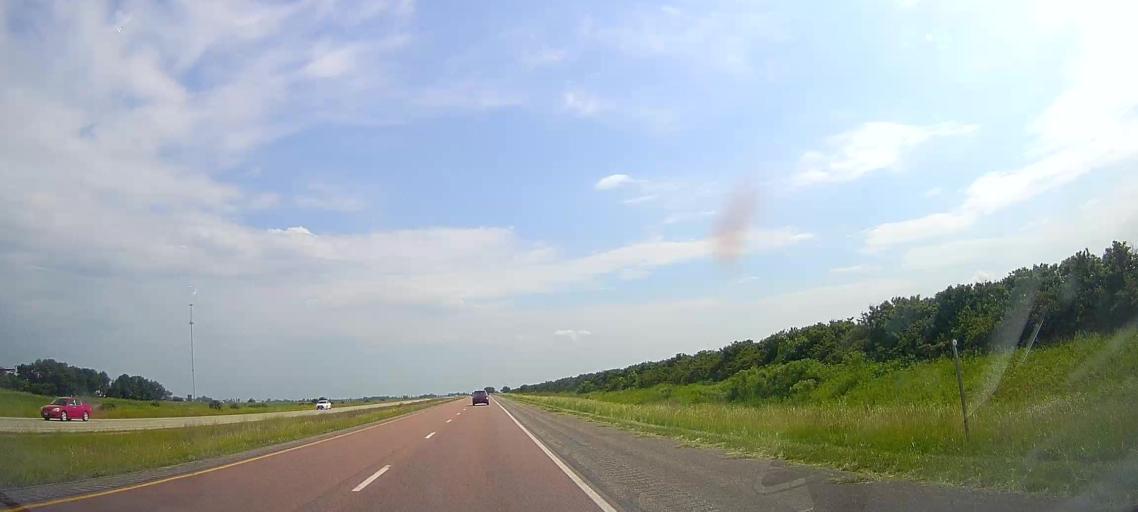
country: US
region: Iowa
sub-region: Monona County
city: Onawa
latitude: 41.9594
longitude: -96.1030
